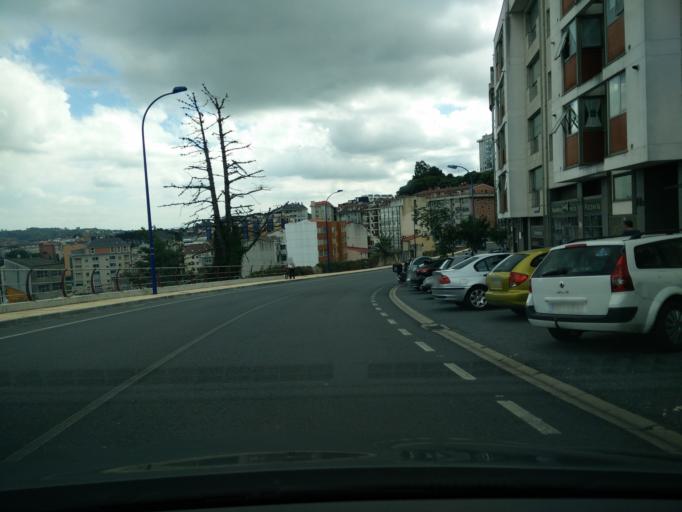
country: ES
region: Galicia
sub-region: Provincia da Coruna
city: Culleredo
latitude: 43.3243
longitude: -8.3817
